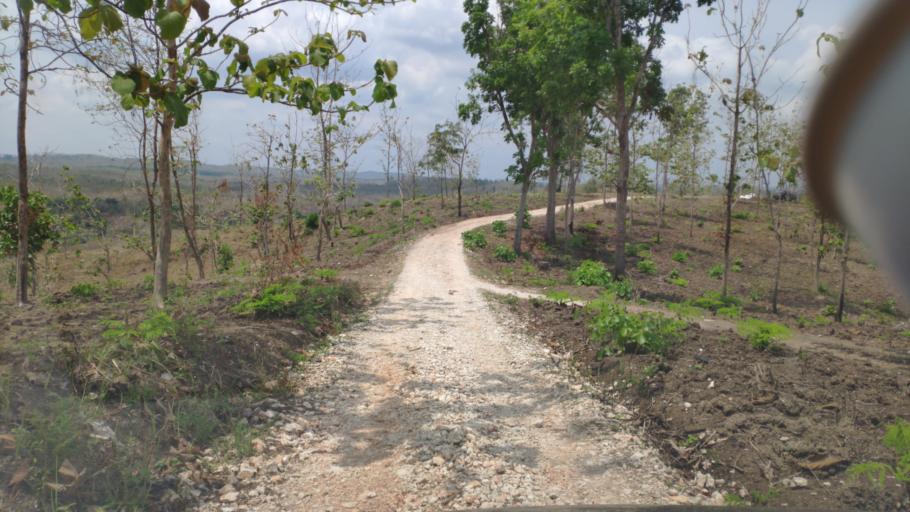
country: ID
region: Central Java
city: Klopoduwur
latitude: -7.0503
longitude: 111.4041
